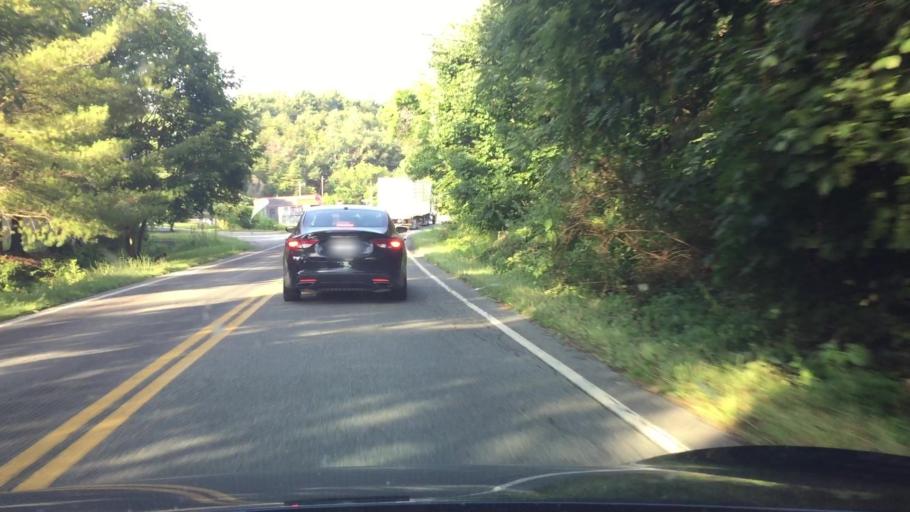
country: US
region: Virginia
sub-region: City of Radford
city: Radford
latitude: 37.1280
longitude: -80.5103
